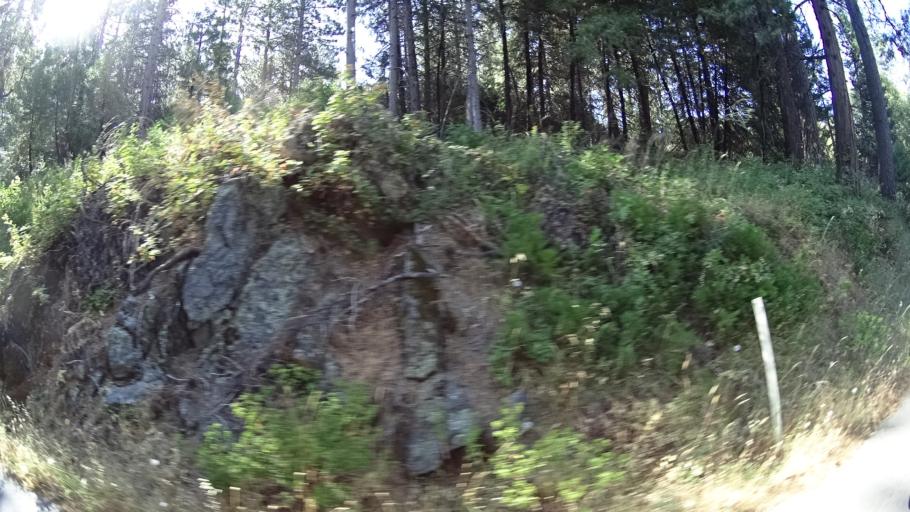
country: US
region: California
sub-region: Amador County
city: Pioneer
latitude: 38.3969
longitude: -120.5759
